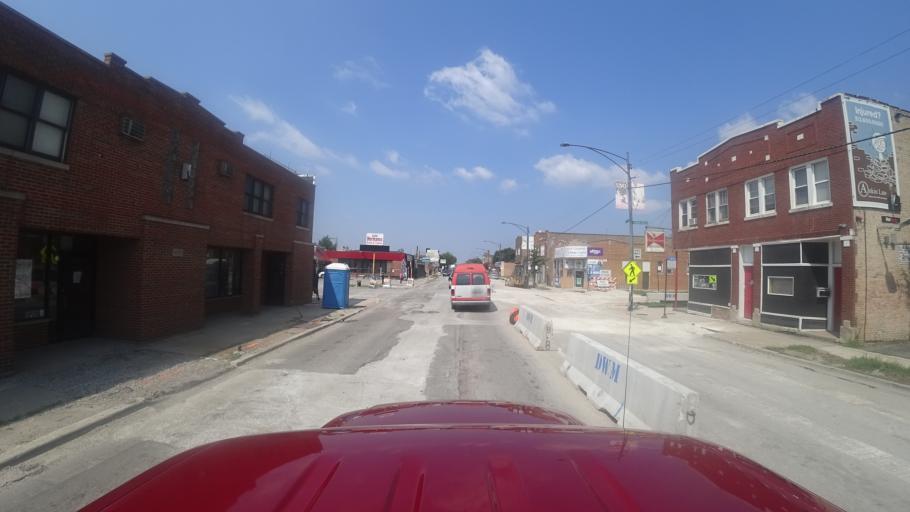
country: US
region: Illinois
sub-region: Cook County
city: Cicero
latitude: 41.8079
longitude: -87.7257
